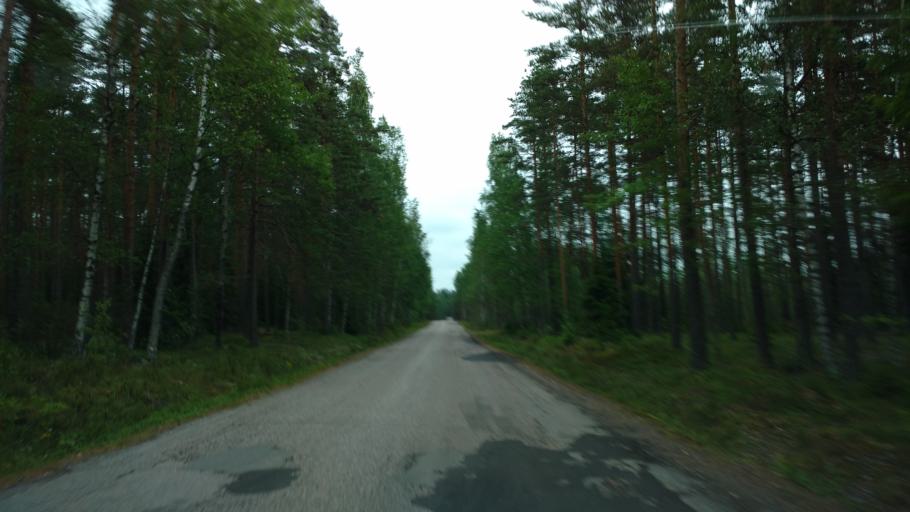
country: FI
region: Varsinais-Suomi
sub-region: Salo
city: Kiikala
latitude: 60.4752
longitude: 23.6589
